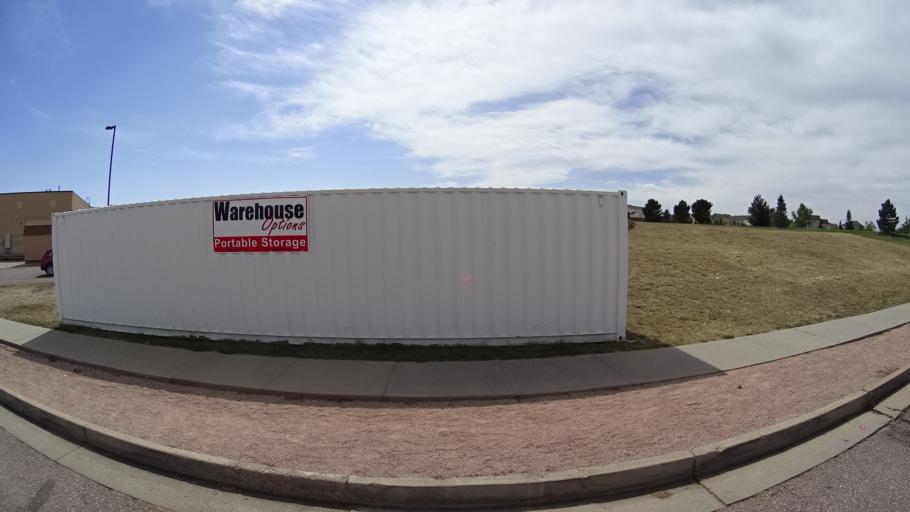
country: US
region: Colorado
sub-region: El Paso County
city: Cimarron Hills
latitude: 38.9070
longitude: -104.7125
